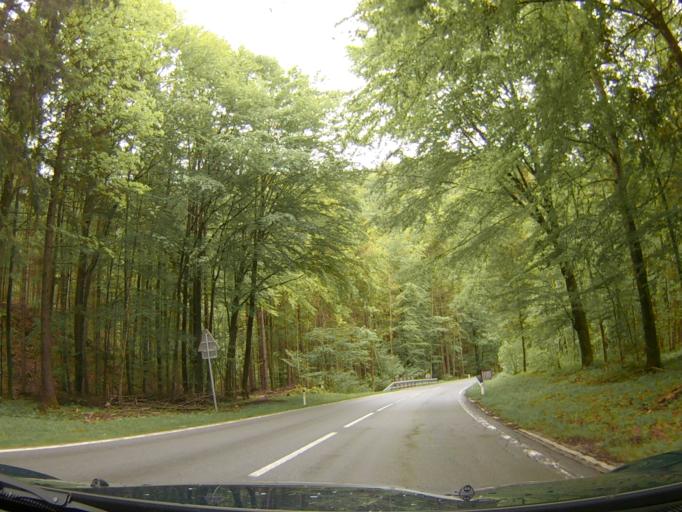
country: AT
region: Upper Austria
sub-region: Politischer Bezirk Vocklabruck
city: Sankt Lorenz
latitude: 47.7919
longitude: 13.3982
